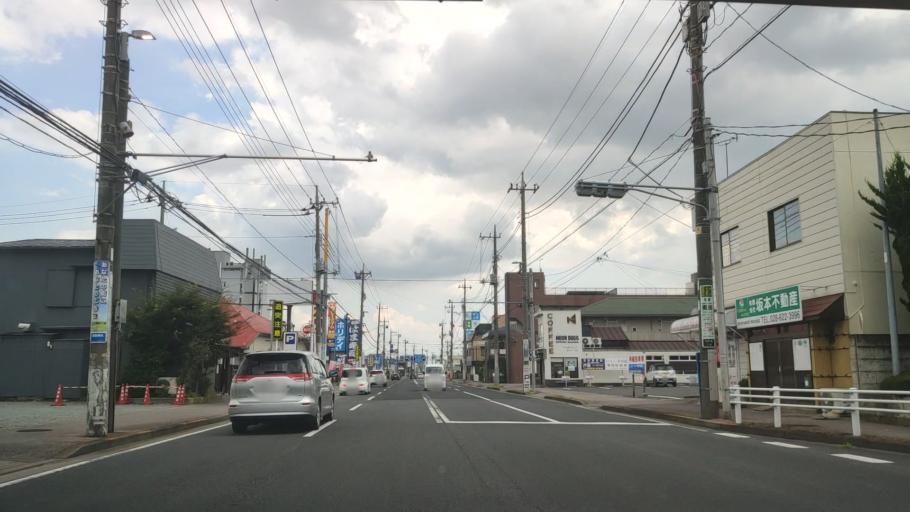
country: JP
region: Tochigi
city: Utsunomiya-shi
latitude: 36.5778
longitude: 139.8703
